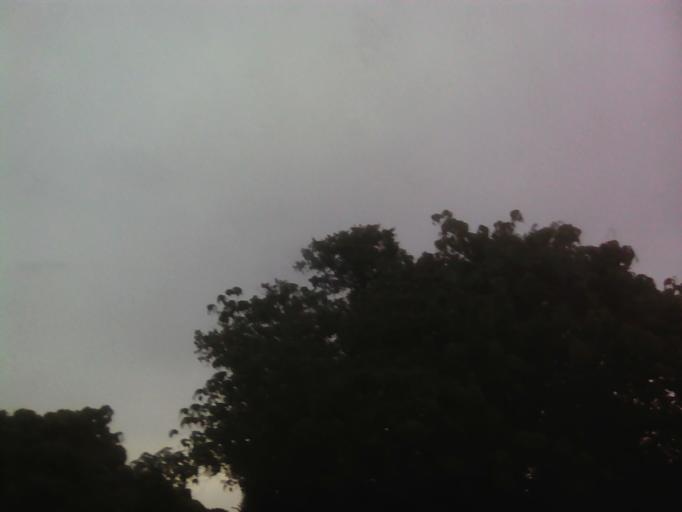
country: MY
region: Penang
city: Perai
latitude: 5.3983
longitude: 100.4122
